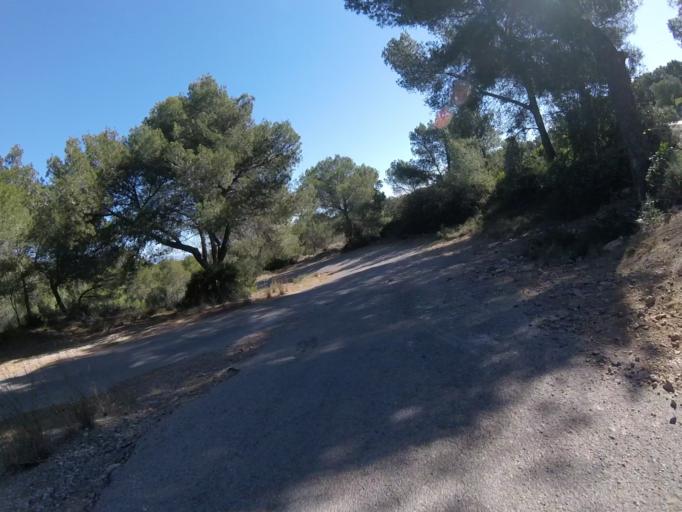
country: ES
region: Valencia
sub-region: Provincia de Castello
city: Orpesa/Oropesa del Mar
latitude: 40.0743
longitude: 0.1110
